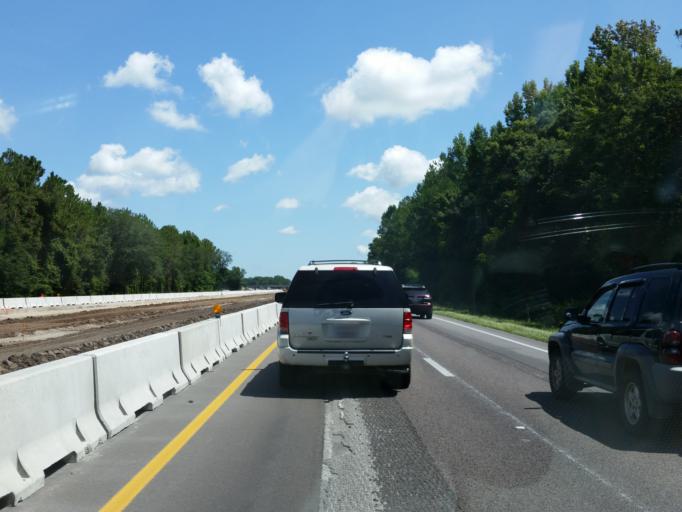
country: US
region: Florida
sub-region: Pasco County
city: San Antonio
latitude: 28.3492
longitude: -82.3209
